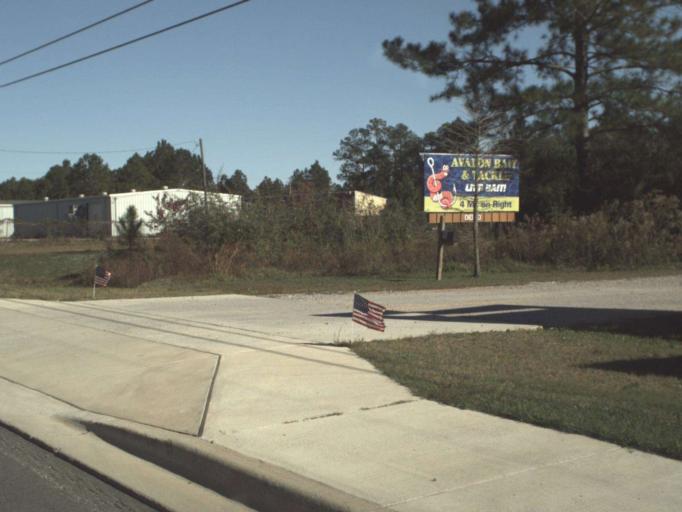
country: US
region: Florida
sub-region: Santa Rosa County
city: Bagdad
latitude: 30.5409
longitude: -87.0872
